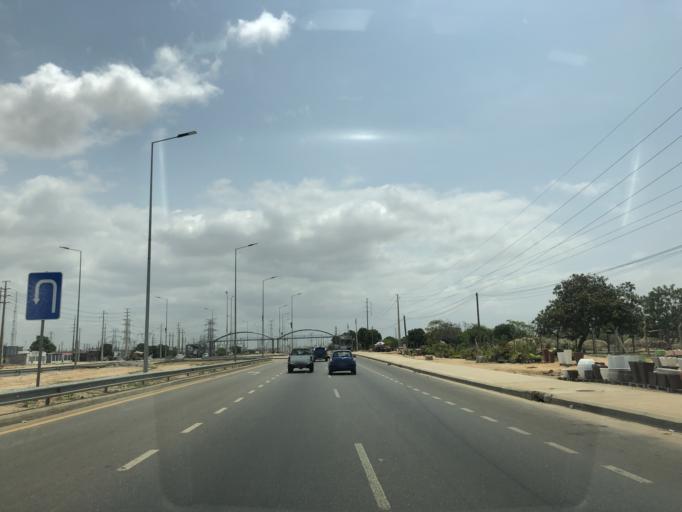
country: AO
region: Luanda
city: Luanda
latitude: -8.9648
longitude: 13.2558
